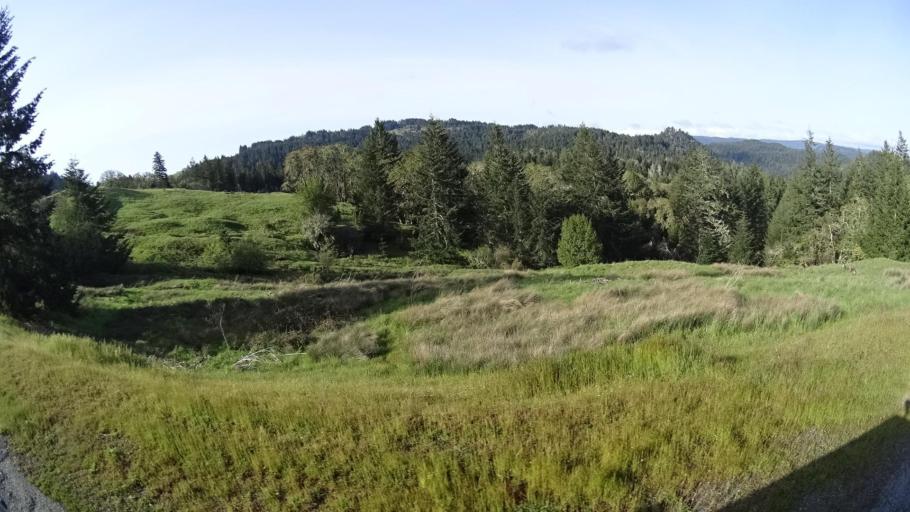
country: US
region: California
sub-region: Humboldt County
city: Hydesville
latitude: 40.6618
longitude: -123.9286
